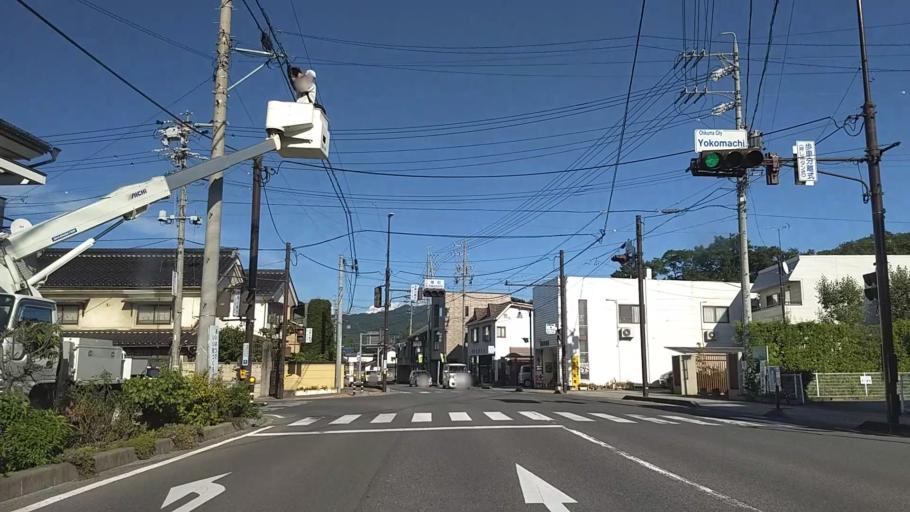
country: JP
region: Nagano
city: Nagano-shi
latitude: 36.5388
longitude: 138.1269
